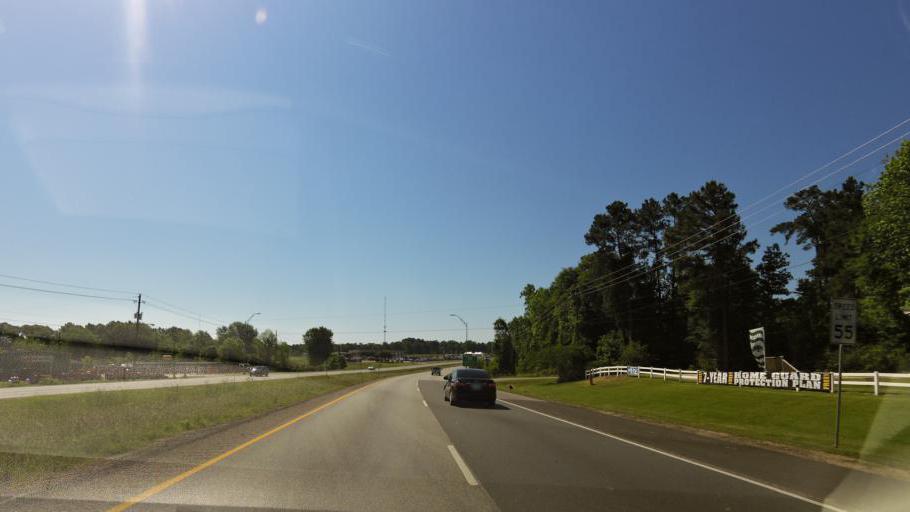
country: US
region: Texas
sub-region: Angelina County
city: Lufkin
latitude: 31.3462
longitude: -94.6935
